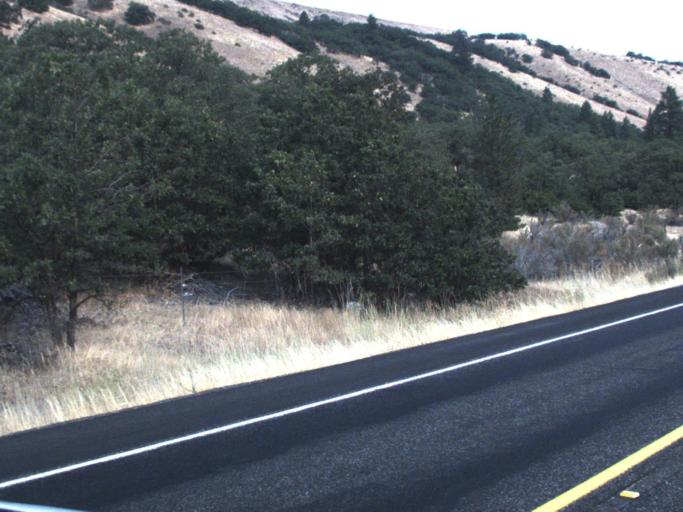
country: US
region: Washington
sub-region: Klickitat County
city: Goldendale
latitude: 46.0599
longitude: -120.5656
